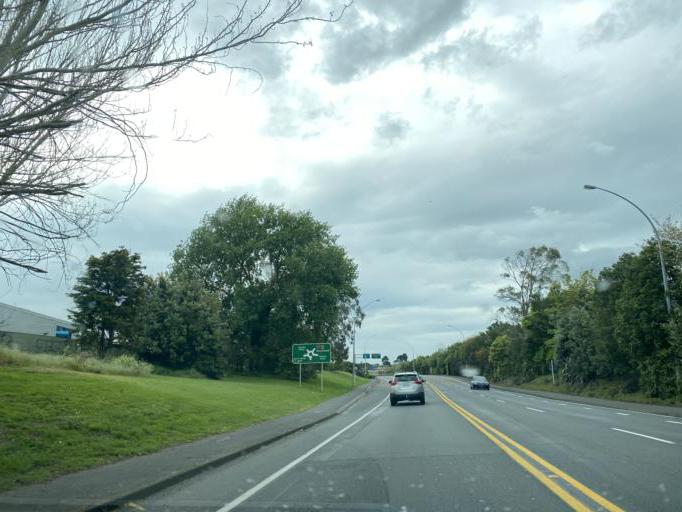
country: NZ
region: Waikato
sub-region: Hamilton City
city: Hamilton
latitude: -37.7849
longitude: 175.2550
